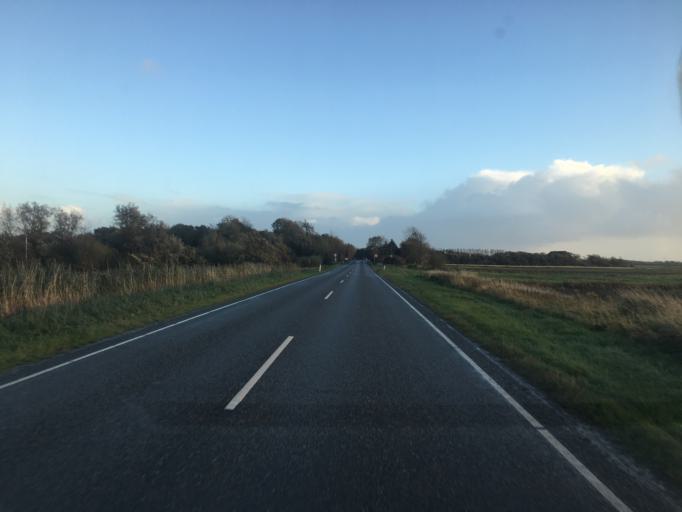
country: DE
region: Schleswig-Holstein
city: Neukirchen
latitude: 54.9093
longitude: 8.7467
